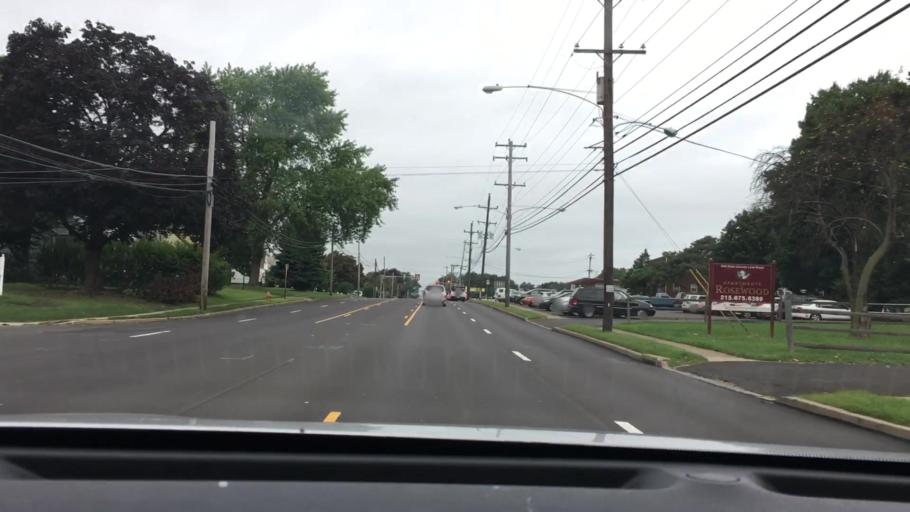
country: US
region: Pennsylvania
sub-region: Bucks County
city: Warminster Heights
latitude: 40.1786
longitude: -75.0837
